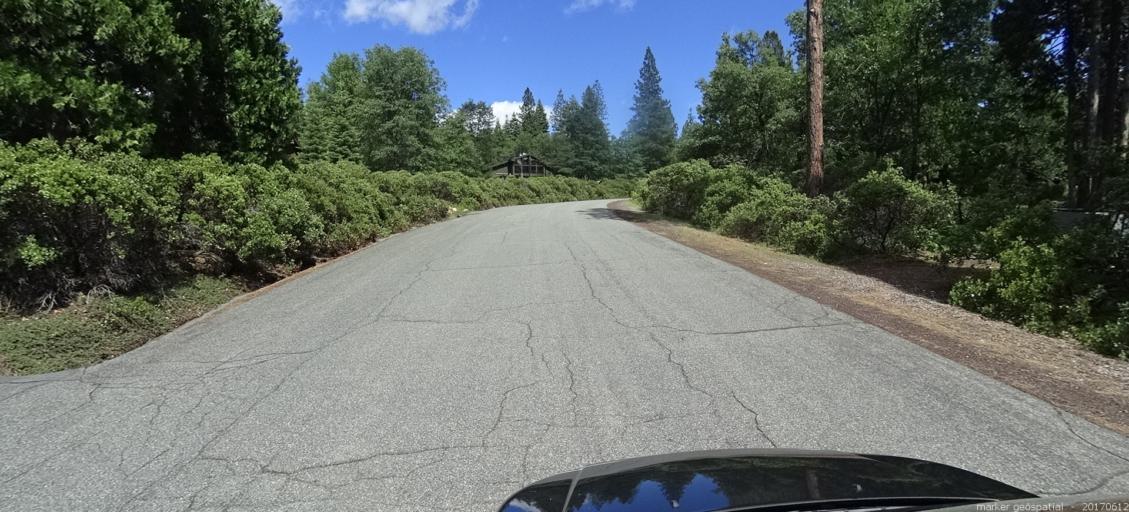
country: US
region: California
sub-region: Siskiyou County
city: Mount Shasta
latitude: 41.3174
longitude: -122.2865
